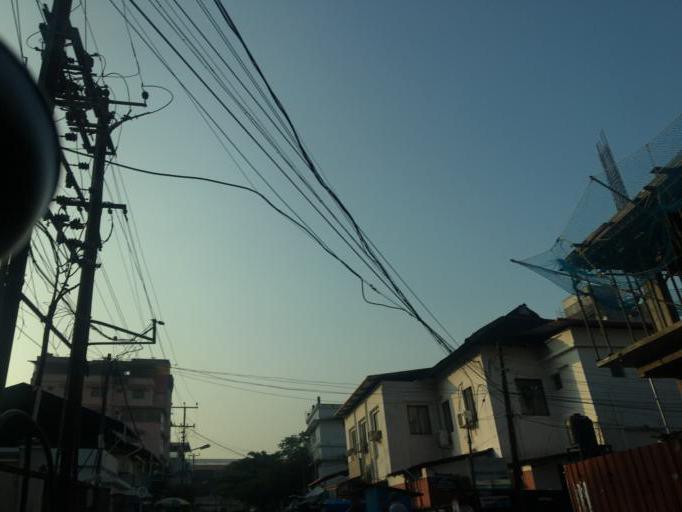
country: IN
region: Kerala
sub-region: Ernakulam
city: Cochin
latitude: 9.9734
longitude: 76.2811
